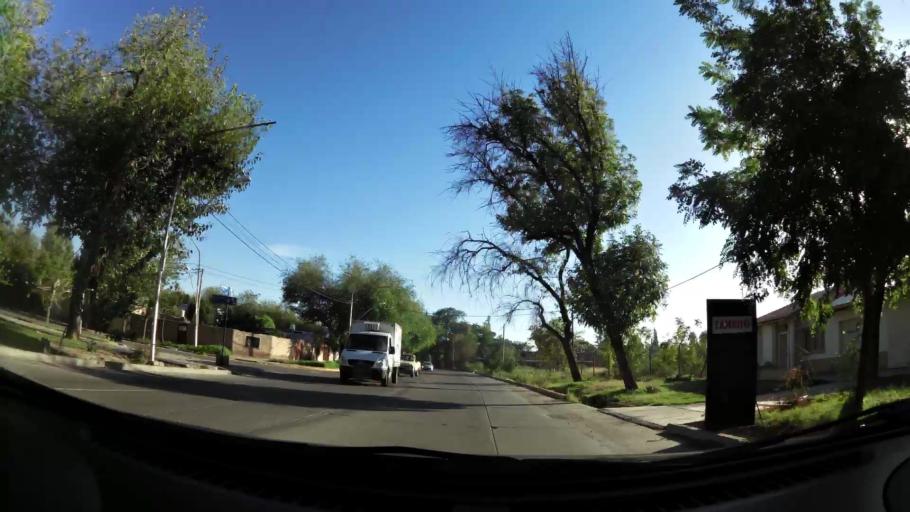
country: AR
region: Mendoza
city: Las Heras
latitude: -32.8689
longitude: -68.8177
